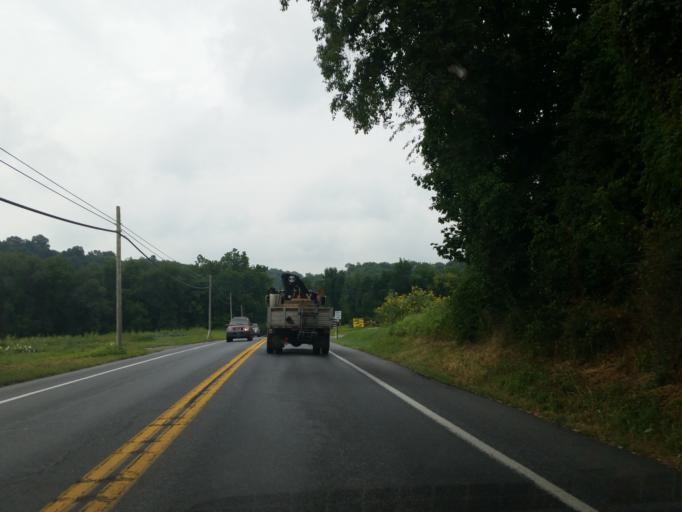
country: US
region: Pennsylvania
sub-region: Lancaster County
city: Brickerville
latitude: 40.2014
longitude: -76.3005
